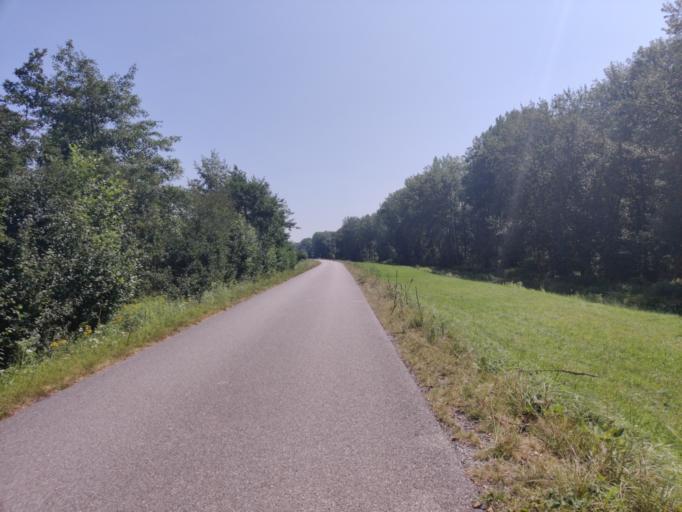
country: AT
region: Upper Austria
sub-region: Politischer Bezirk Urfahr-Umgebung
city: Feldkirchen an der Donau
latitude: 48.3173
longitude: 14.0675
